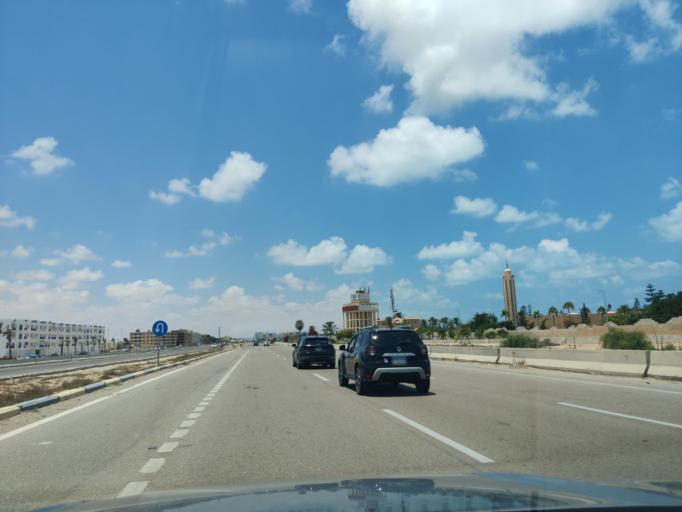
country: EG
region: Muhafazat Matruh
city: Al `Alamayn
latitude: 30.8164
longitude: 29.0336
